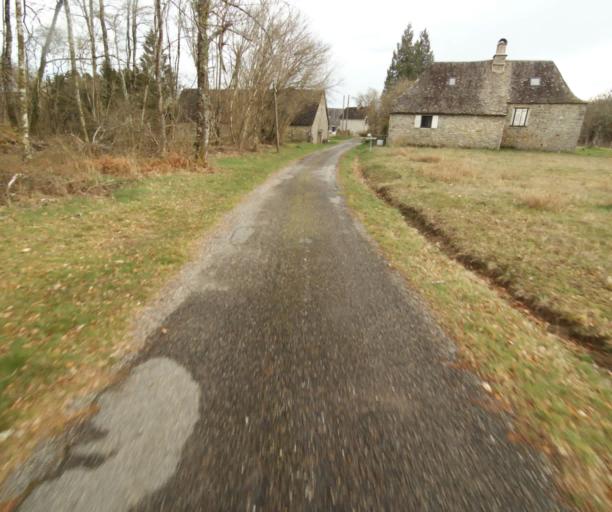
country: FR
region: Limousin
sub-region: Departement de la Correze
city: Saint-Privat
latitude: 45.2190
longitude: 2.0084
